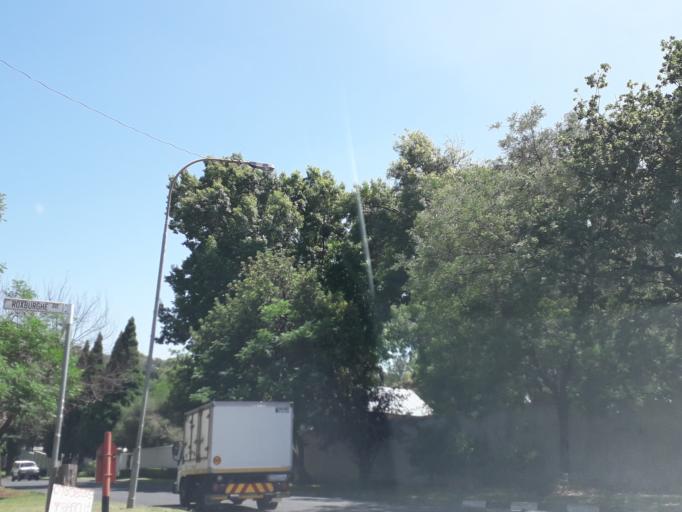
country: ZA
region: Gauteng
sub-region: City of Johannesburg Metropolitan Municipality
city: Johannesburg
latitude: -26.1343
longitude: 28.0297
